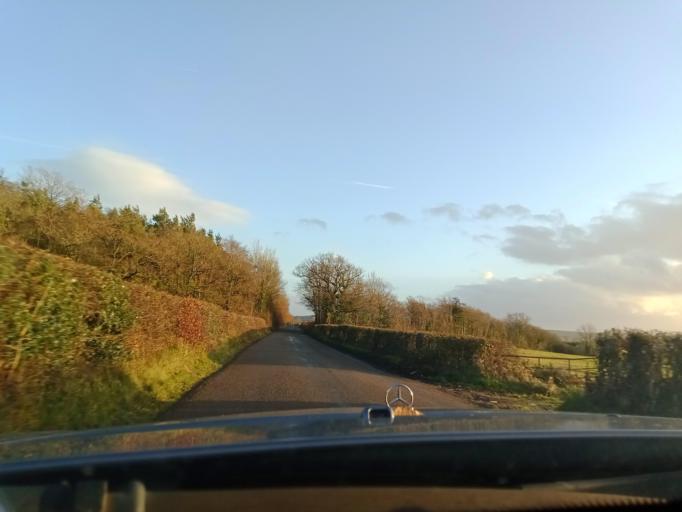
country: IE
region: Leinster
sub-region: Kilkenny
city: Callan
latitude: 52.4945
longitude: -7.3310
